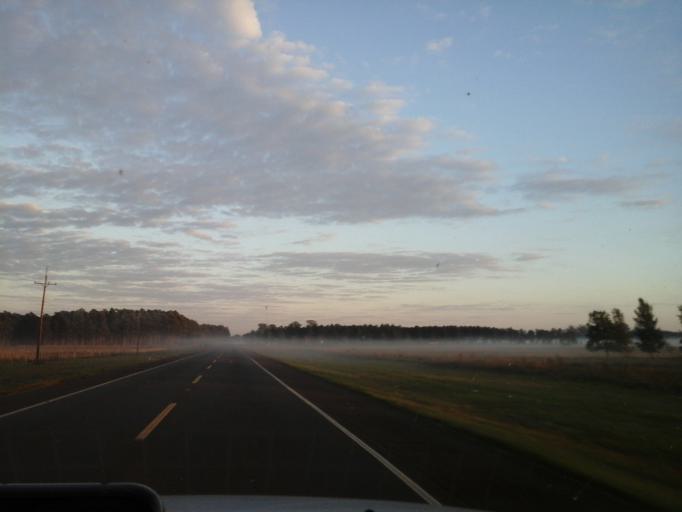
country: PY
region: Itapua
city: General Delgado
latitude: -27.0641
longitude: -56.6208
